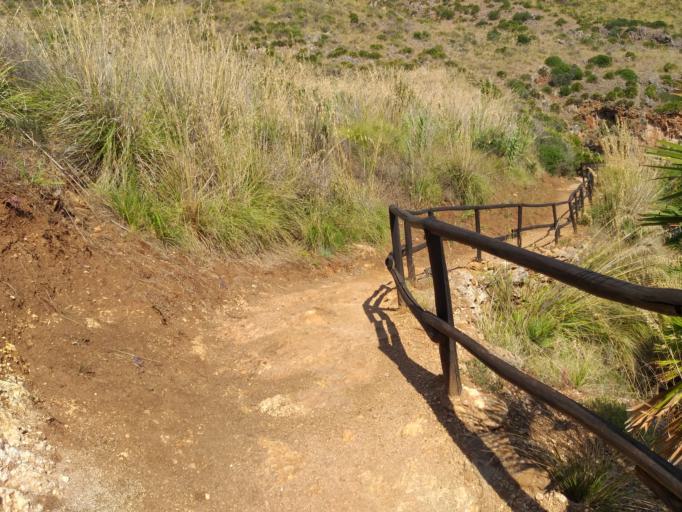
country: IT
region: Sicily
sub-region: Trapani
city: Castelluzzo
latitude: 38.0869
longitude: 12.8054
